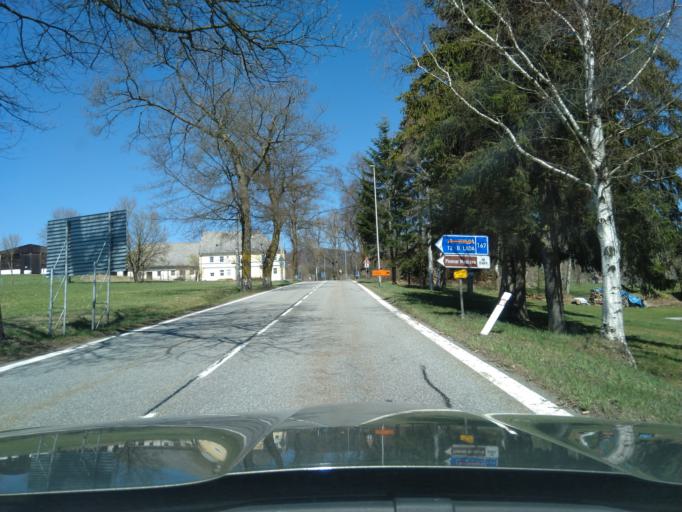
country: CZ
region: Jihocesky
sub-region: Okres Prachatice
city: Borova Lada
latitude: 48.9592
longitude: 13.7575
